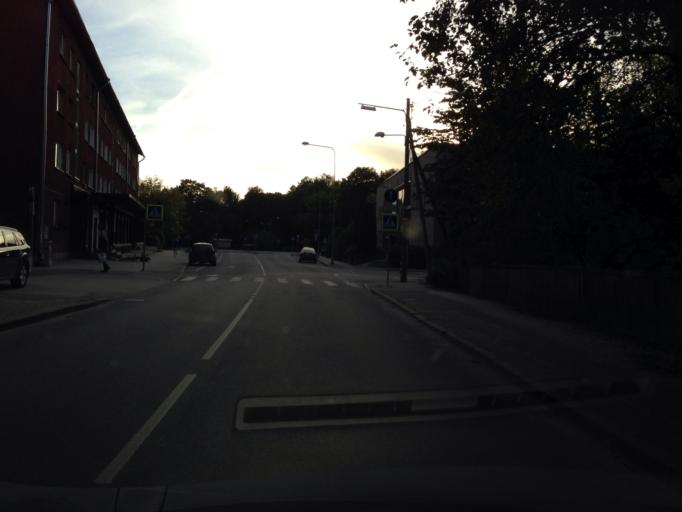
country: EE
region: Tartu
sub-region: Tartu linn
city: Tartu
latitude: 58.3764
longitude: 26.7130
